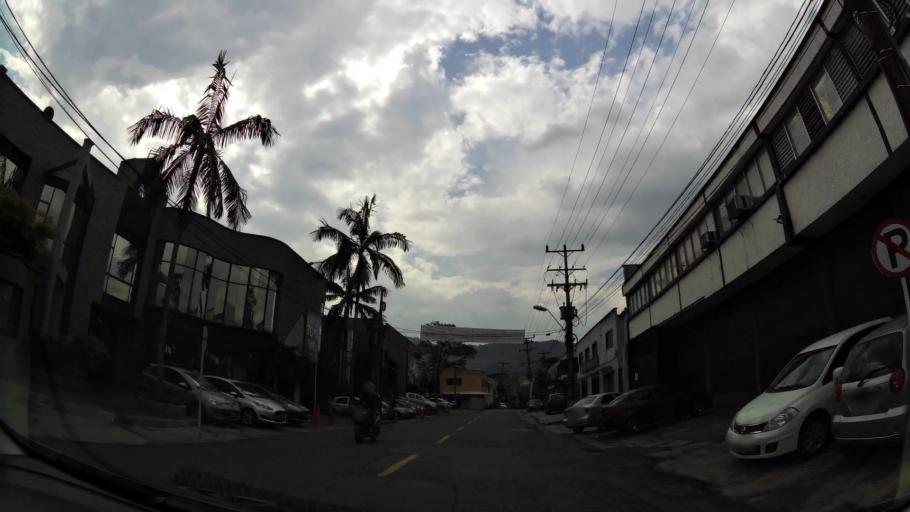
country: CO
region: Antioquia
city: Envigado
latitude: 6.1804
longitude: -75.5947
